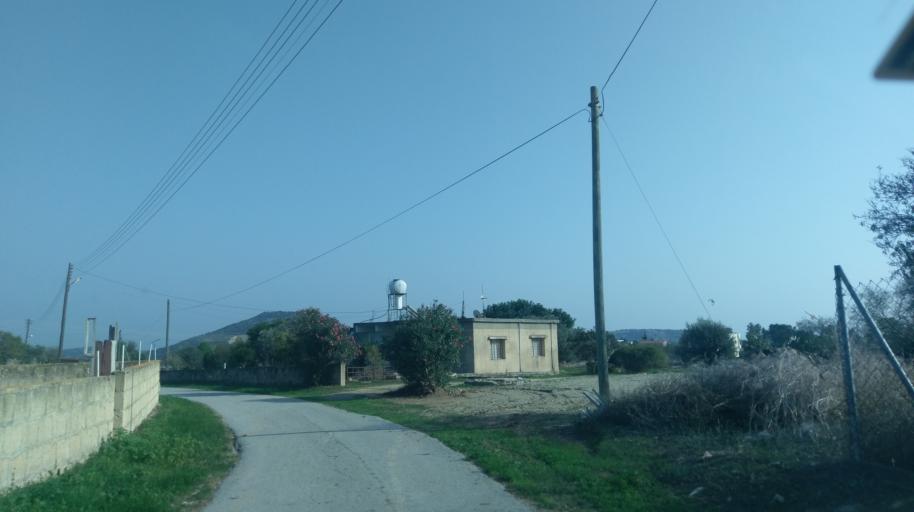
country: CY
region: Ammochostos
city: Rizokarpaso
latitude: 35.5149
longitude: 34.2714
